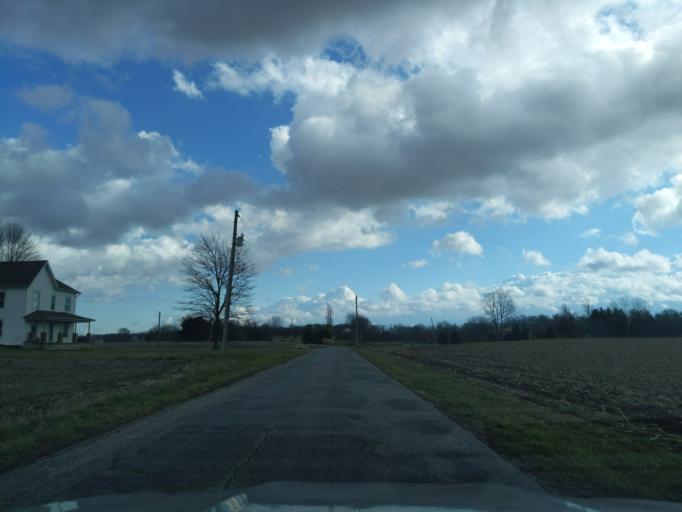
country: US
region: Indiana
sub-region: Decatur County
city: Greensburg
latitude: 39.4093
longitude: -85.5236
